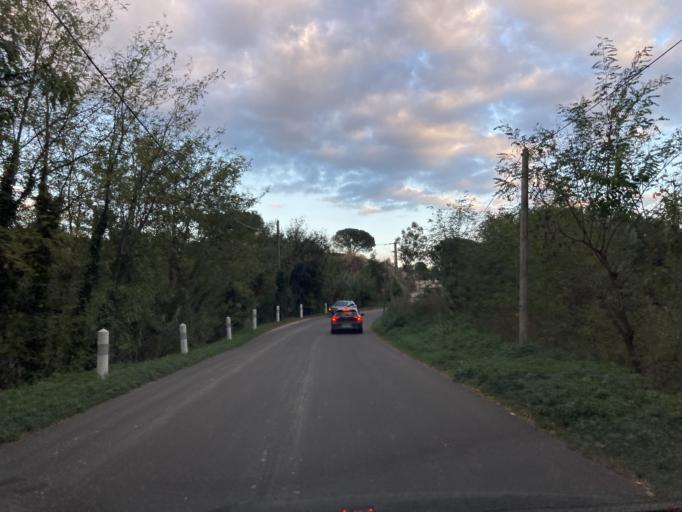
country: FR
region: Languedoc-Roussillon
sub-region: Departement des Pyrenees-Orientales
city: Banyuls-dels-Aspres
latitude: 42.5556
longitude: 2.8610
